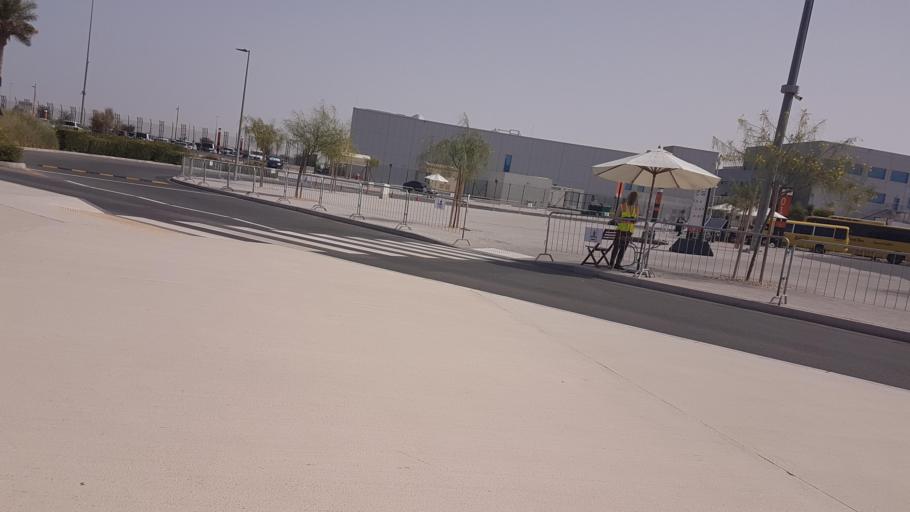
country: AE
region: Dubai
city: Dubai
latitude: 24.9664
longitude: 55.1562
